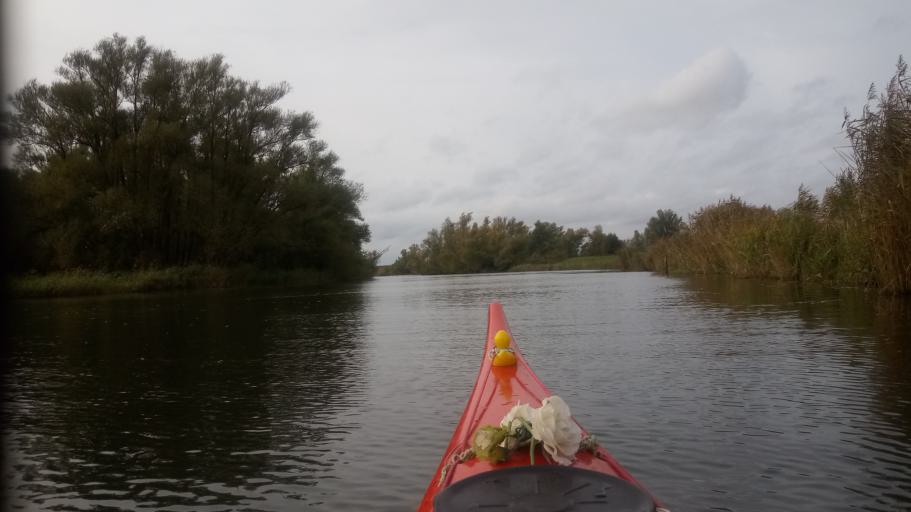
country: NL
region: North Brabant
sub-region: Gemeente Made en Drimmelen
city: Drimmelen
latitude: 51.7318
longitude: 4.7910
